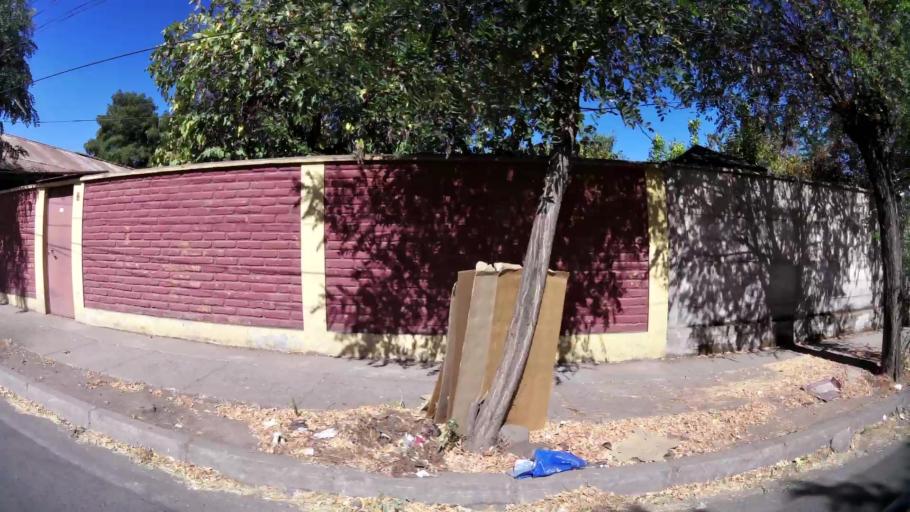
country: CL
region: O'Higgins
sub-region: Provincia de Colchagua
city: Chimbarongo
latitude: -34.5886
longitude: -70.9994
